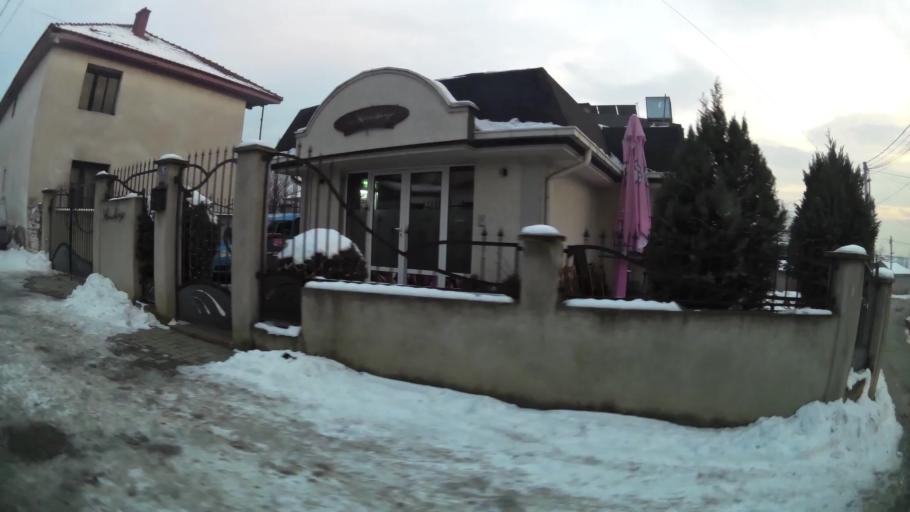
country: MK
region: Suto Orizari
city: Suto Orizare
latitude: 42.0364
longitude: 21.4090
